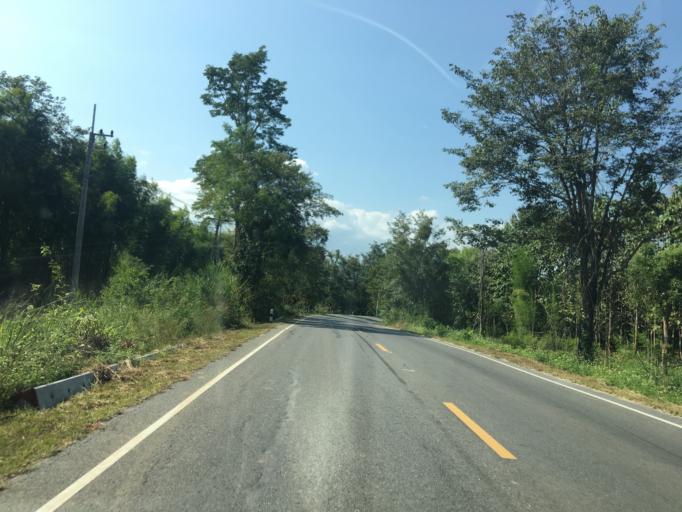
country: TH
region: Phayao
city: Chiang Muan
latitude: 18.8609
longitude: 100.3129
